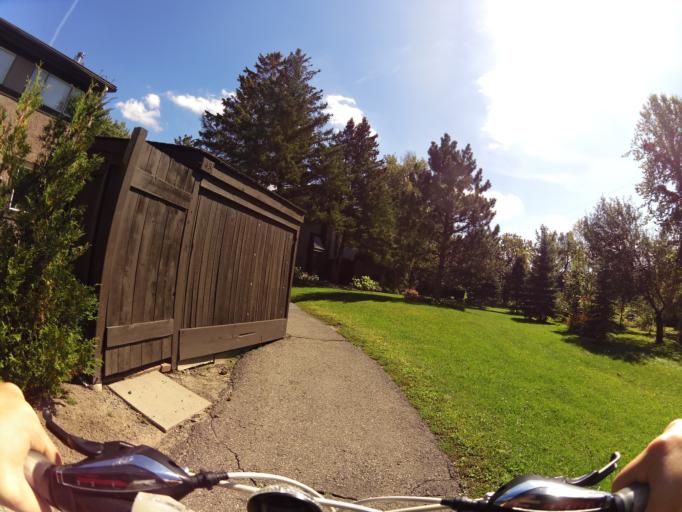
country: CA
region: Ontario
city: Bells Corners
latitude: 45.3203
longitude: -75.9023
